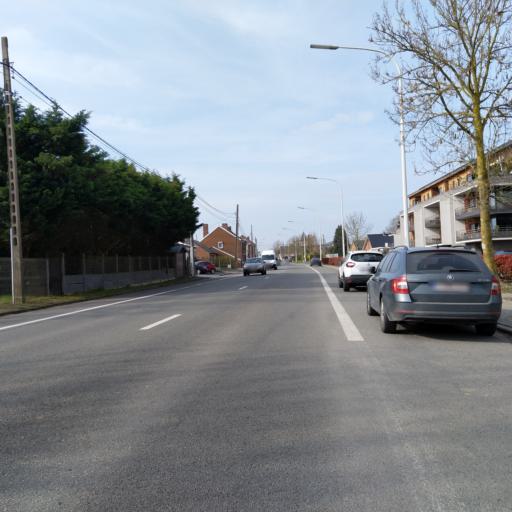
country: BE
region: Wallonia
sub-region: Province du Hainaut
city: Chasse Royale
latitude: 50.4220
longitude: 3.9413
